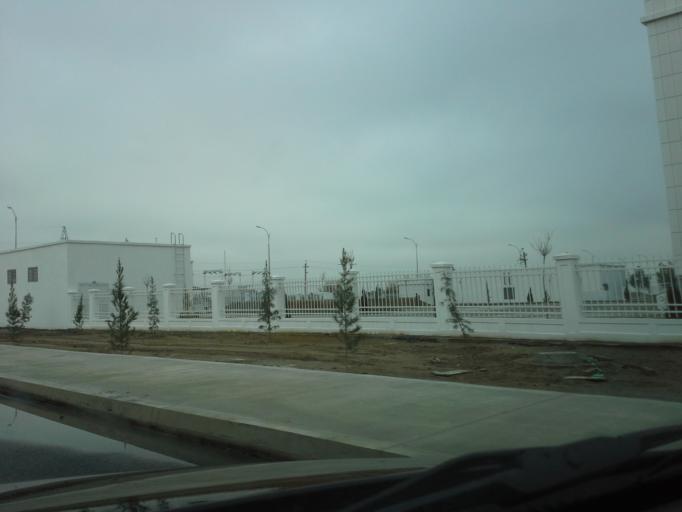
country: TM
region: Ahal
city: Ashgabat
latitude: 37.9658
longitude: 58.4119
